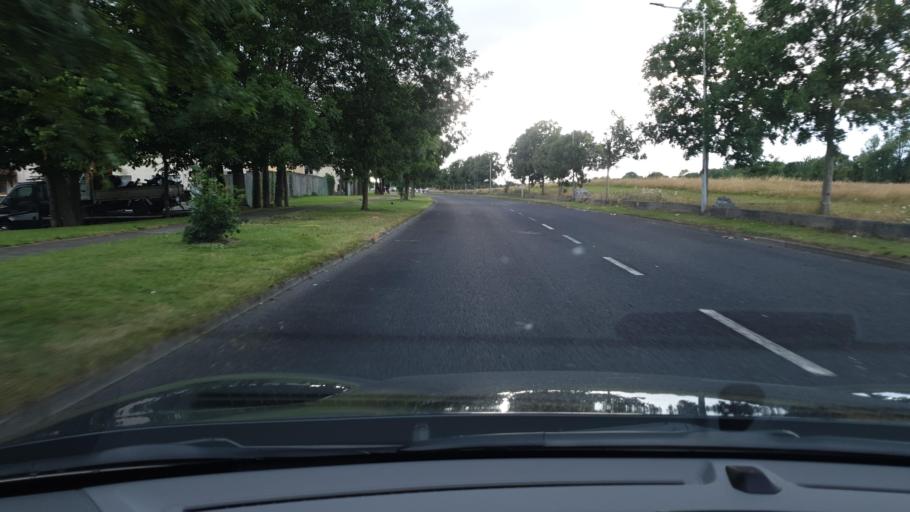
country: IE
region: Leinster
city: Clondalkin
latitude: 53.3285
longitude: -6.4114
